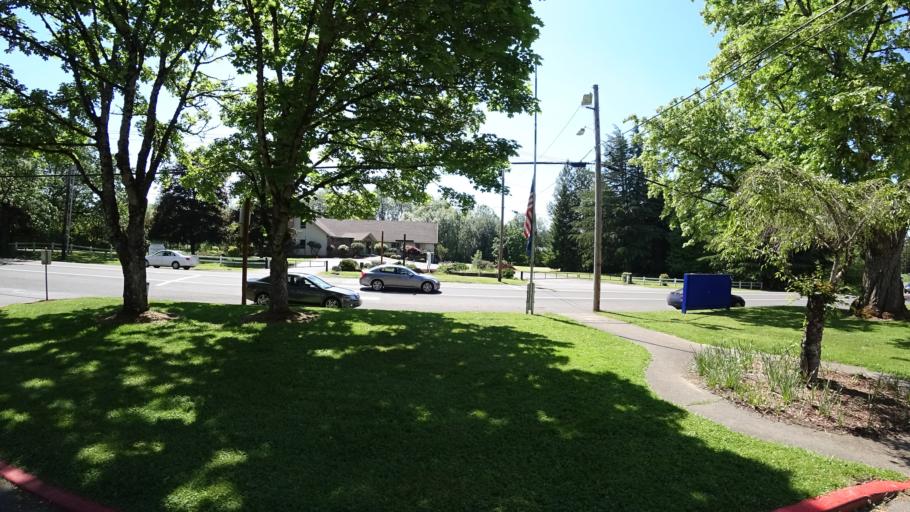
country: US
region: Oregon
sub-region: Clackamas County
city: Damascus
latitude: 45.4644
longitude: -122.4808
